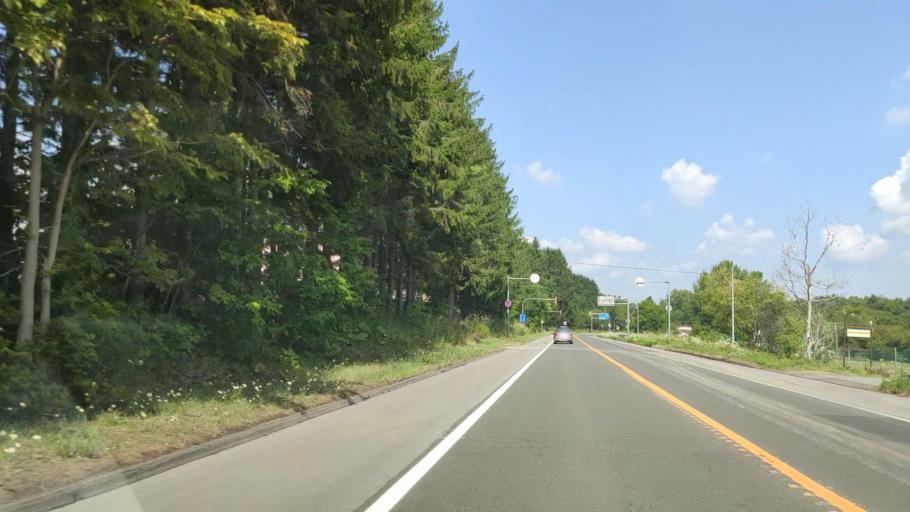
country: JP
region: Hokkaido
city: Shimo-furano
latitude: 43.5129
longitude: 142.4488
